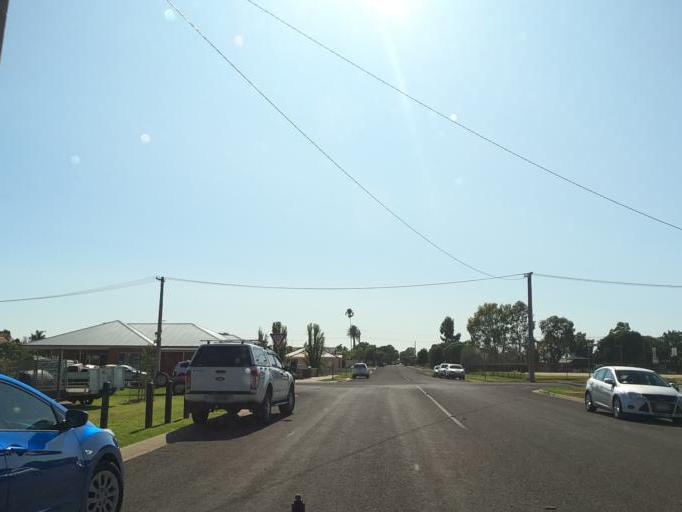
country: AU
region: Victoria
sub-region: Moira
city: Yarrawonga
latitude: -36.0079
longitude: 146.0081
